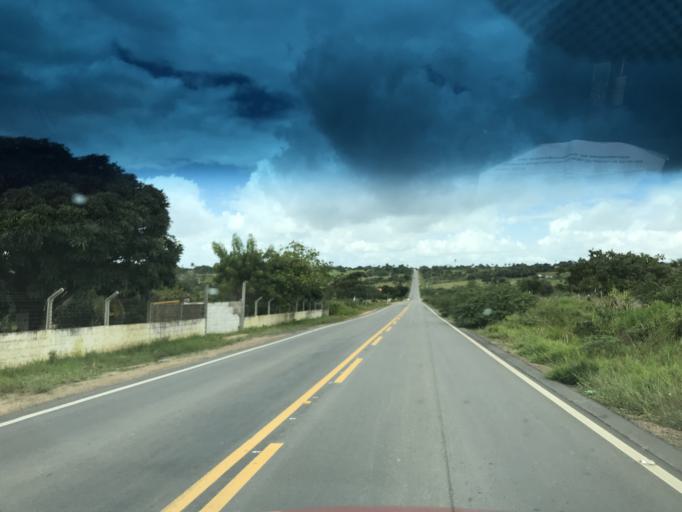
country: BR
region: Bahia
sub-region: Conceicao Do Almeida
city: Conceicao do Almeida
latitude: -12.6852
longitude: -39.2523
